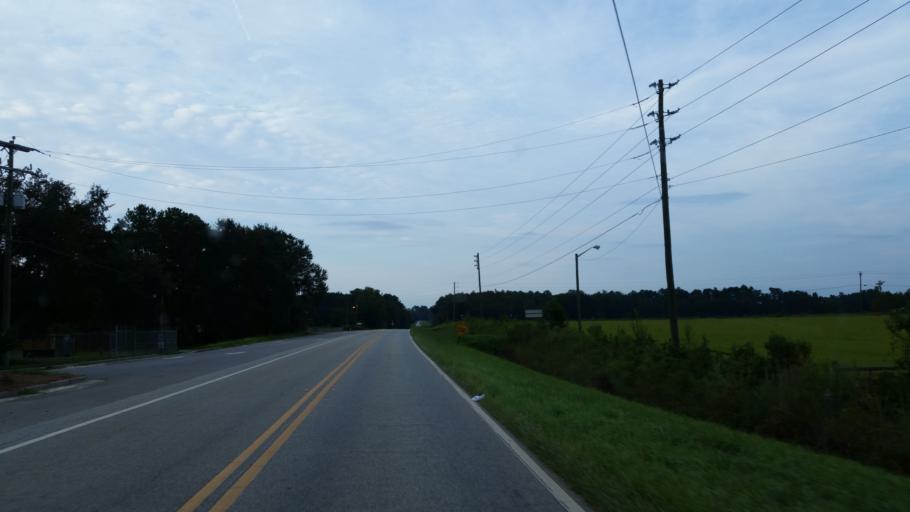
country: US
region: Georgia
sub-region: Lowndes County
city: Valdosta
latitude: 30.7218
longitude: -83.3185
